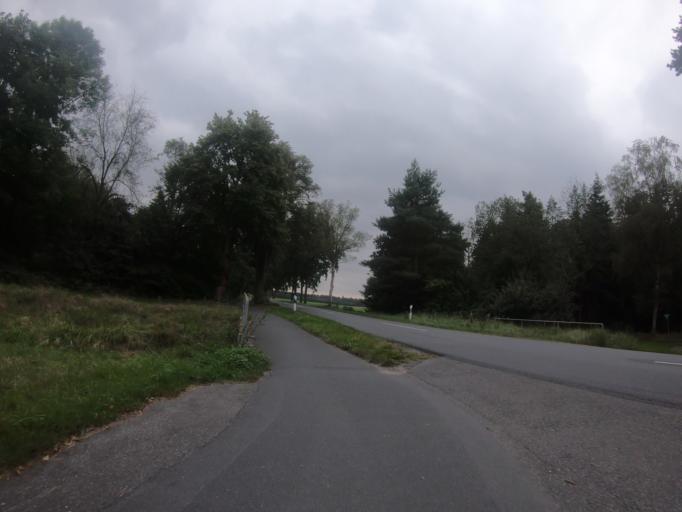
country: DE
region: Lower Saxony
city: Ribbesbuttel
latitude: 52.4452
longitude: 10.5017
